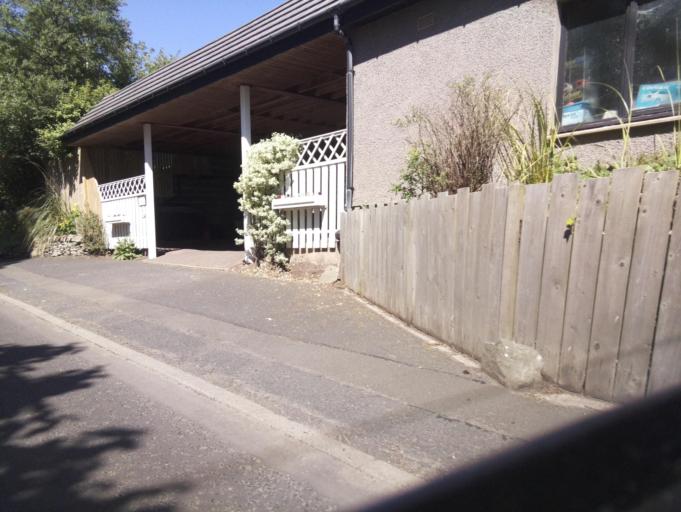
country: GB
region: Scotland
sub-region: The Scottish Borders
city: Galashiels
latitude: 55.6974
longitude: -2.8704
